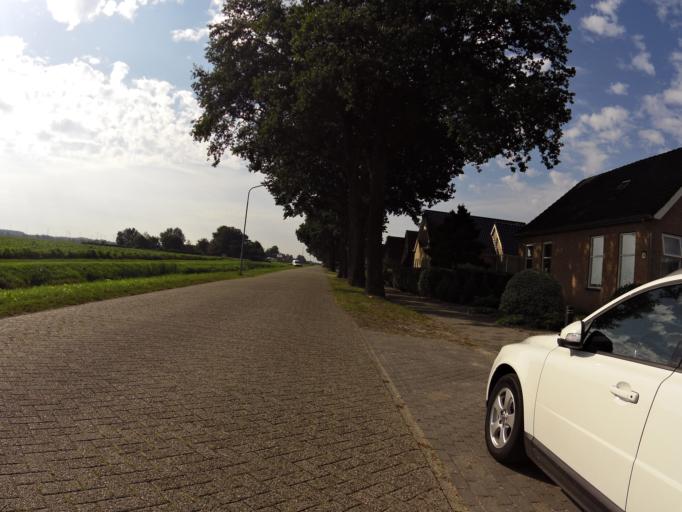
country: NL
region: Drenthe
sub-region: Gemeente Emmen
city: Klazienaveen
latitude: 52.7094
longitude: 7.0458
